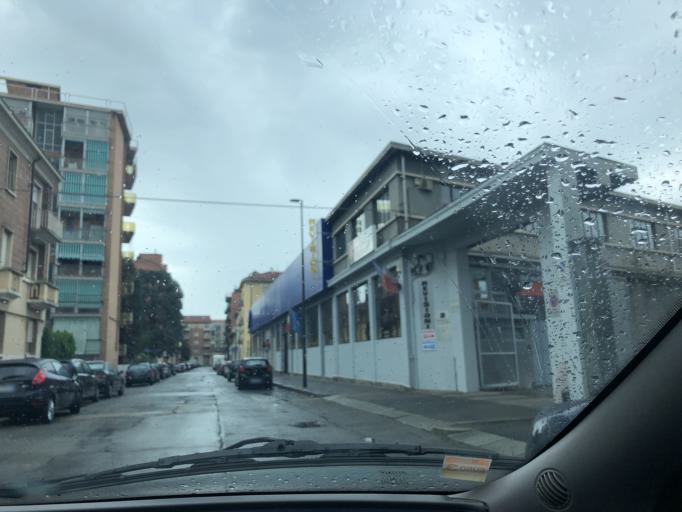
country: IT
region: Piedmont
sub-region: Provincia di Torino
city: Lesna
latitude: 45.0772
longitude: 7.6298
